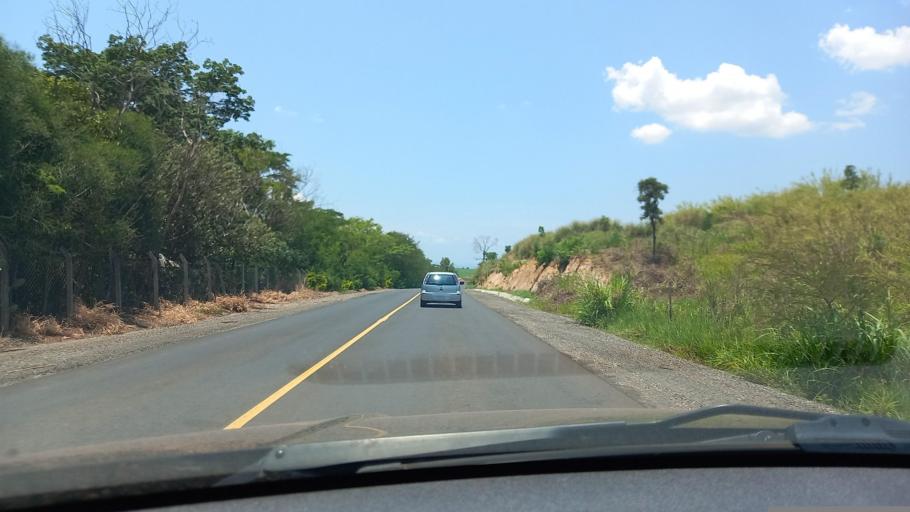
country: BR
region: Sao Paulo
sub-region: Moji-Guacu
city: Mogi-Gaucu
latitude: -22.3525
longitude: -46.8725
